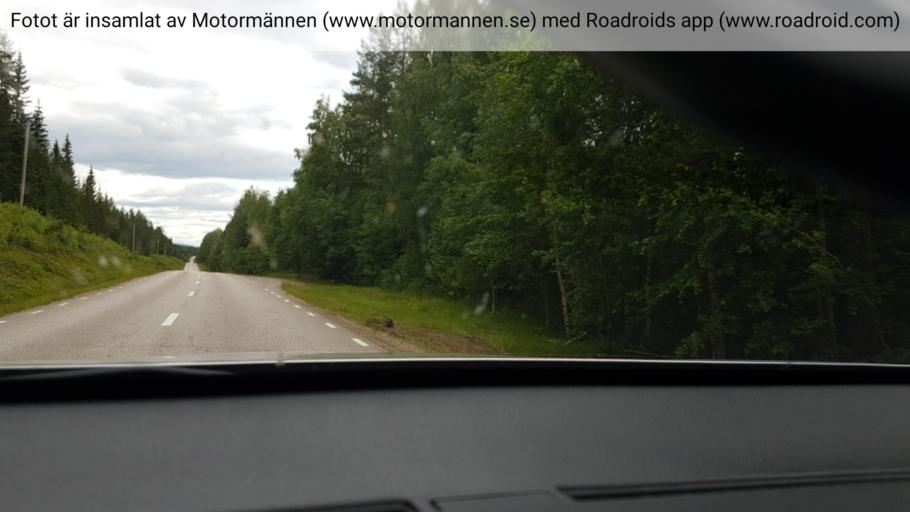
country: NO
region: Hedmark
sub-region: Trysil
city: Innbygda
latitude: 61.0096
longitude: 12.4778
